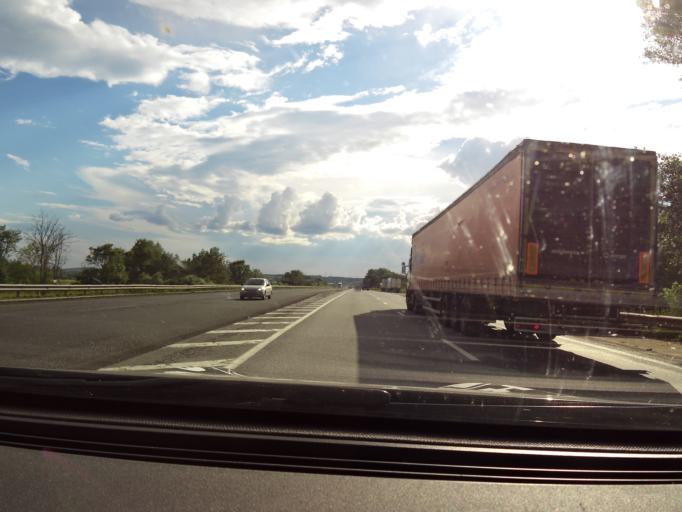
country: RU
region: Vladimir
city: Gorokhovets
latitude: 56.2060
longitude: 42.7275
